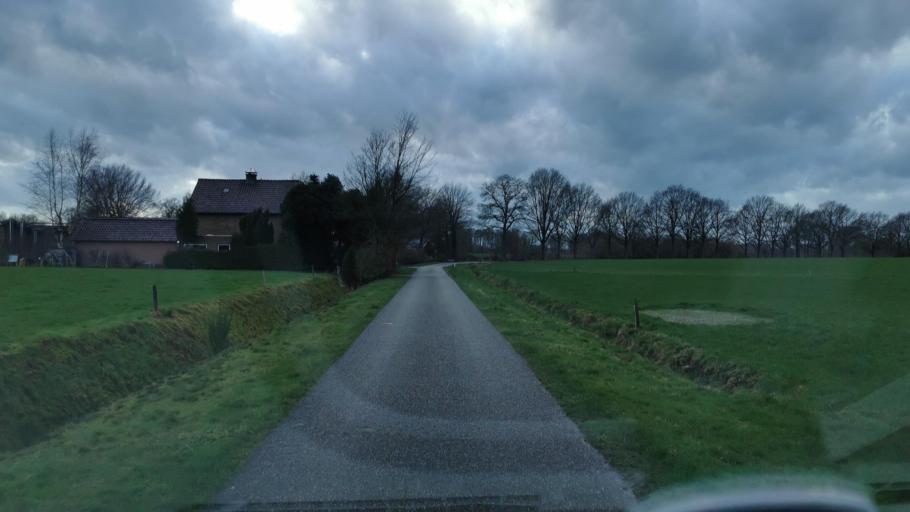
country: DE
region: Lower Saxony
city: Lage
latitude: 52.4205
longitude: 6.9796
